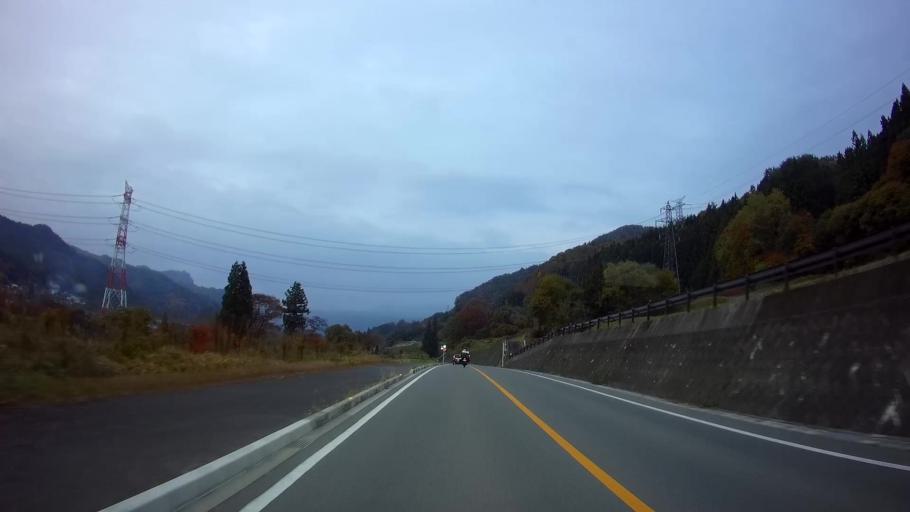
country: JP
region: Gunma
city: Nakanojomachi
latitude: 36.5624
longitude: 138.7513
